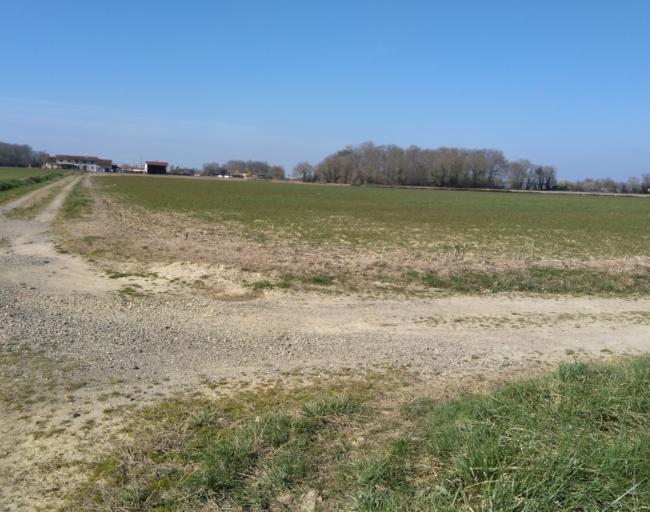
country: FR
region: Midi-Pyrenees
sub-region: Departement du Gers
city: Barcelonne-du-Gers
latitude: 43.6829
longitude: -0.1971
